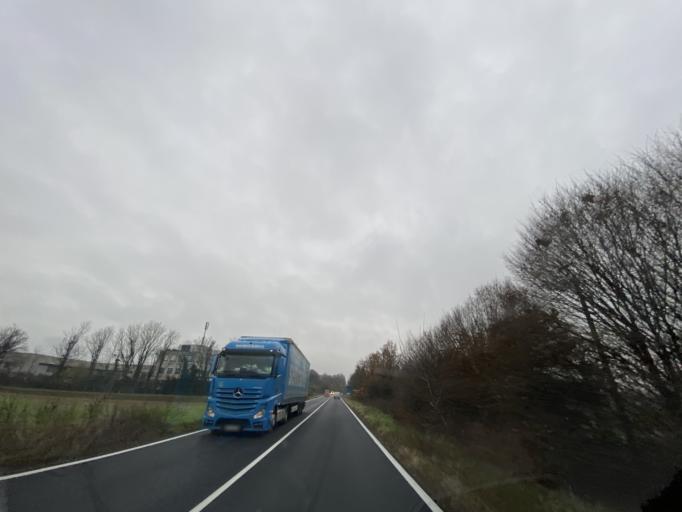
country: IT
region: Lombardy
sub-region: Citta metropolitana di Milano
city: Cusago
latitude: 45.4469
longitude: 9.0439
